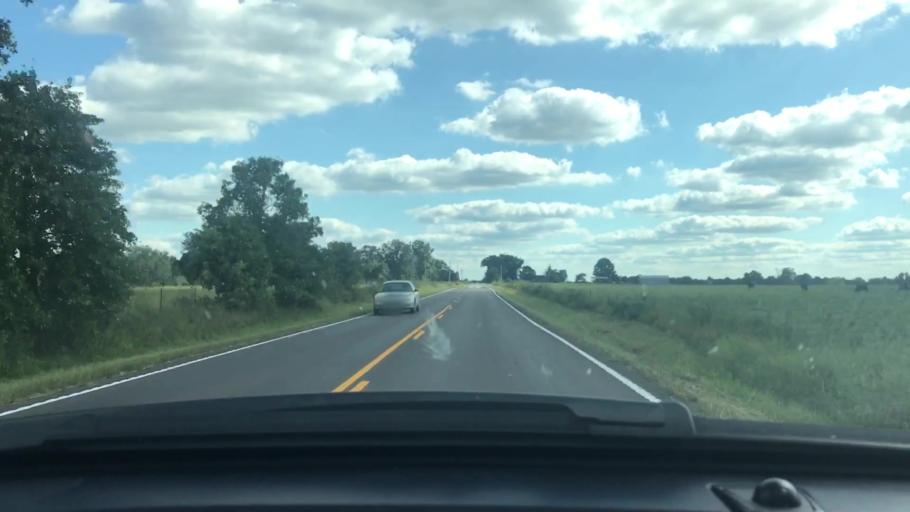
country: US
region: Missouri
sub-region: Wright County
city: Mountain Grove
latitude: 37.2673
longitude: -92.3081
